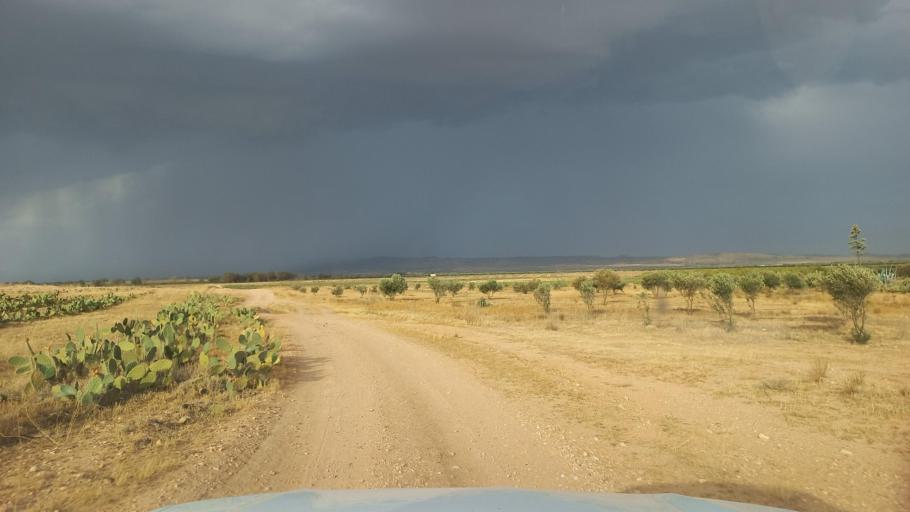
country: TN
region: Al Qasrayn
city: Kasserine
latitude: 35.2875
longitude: 9.0444
